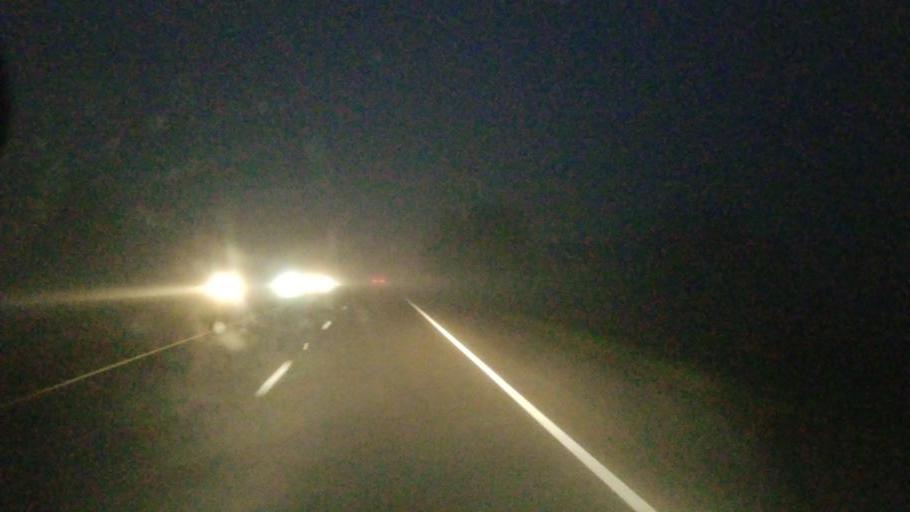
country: US
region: Ohio
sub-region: Ross County
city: Kingston
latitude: 39.4299
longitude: -82.9753
